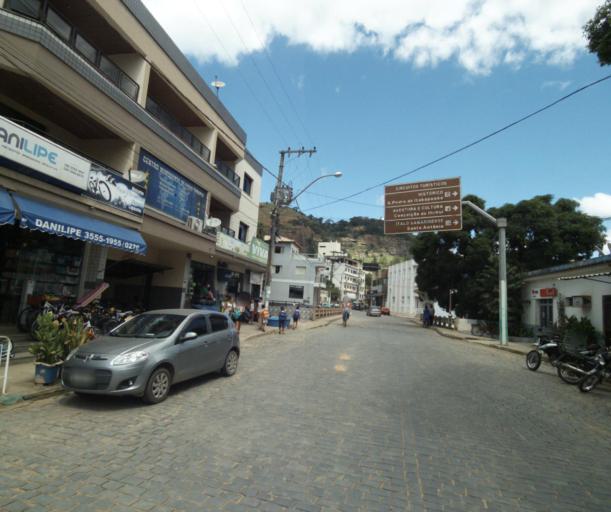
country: BR
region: Espirito Santo
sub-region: Mimoso Do Sul
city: Mimoso do Sul
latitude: -21.0613
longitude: -41.3669
